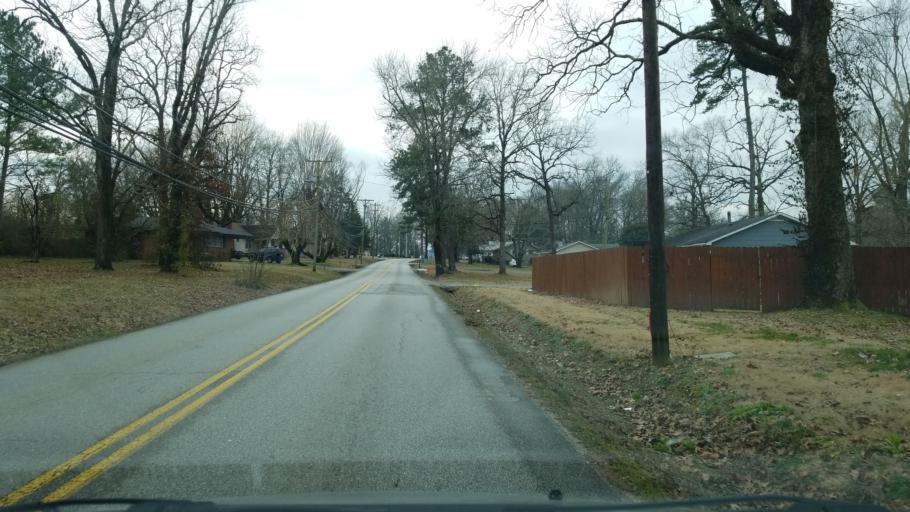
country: US
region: Tennessee
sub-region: Hamilton County
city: East Brainerd
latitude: 34.9998
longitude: -85.1492
